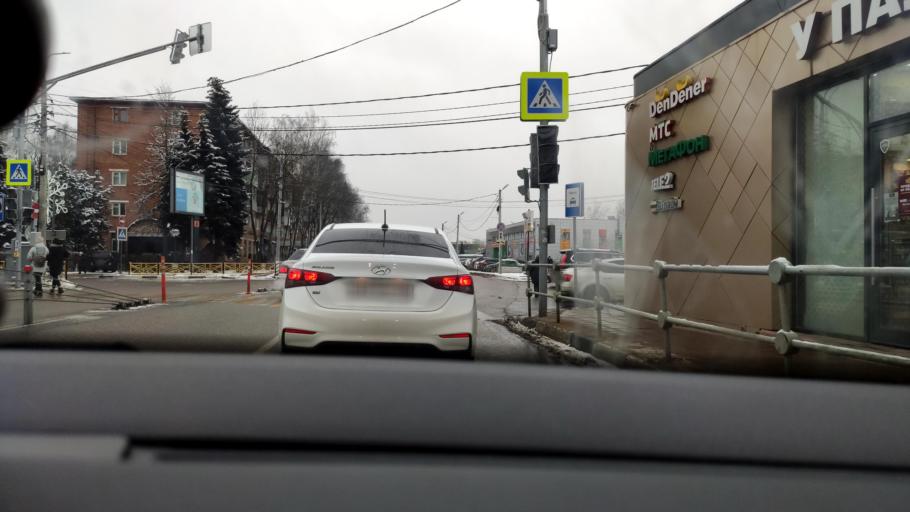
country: RU
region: Moskovskaya
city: Solnechnogorsk
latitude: 56.1846
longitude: 36.9732
